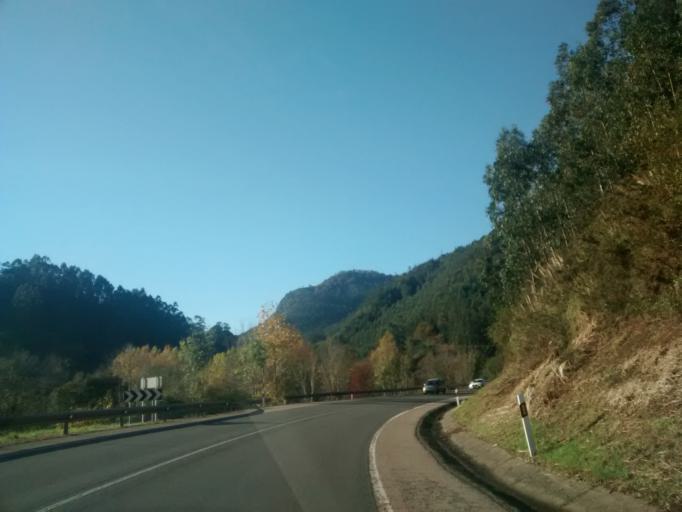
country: ES
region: Cantabria
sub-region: Provincia de Cantabria
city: Puente Viesgo
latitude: 43.3063
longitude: -3.9618
